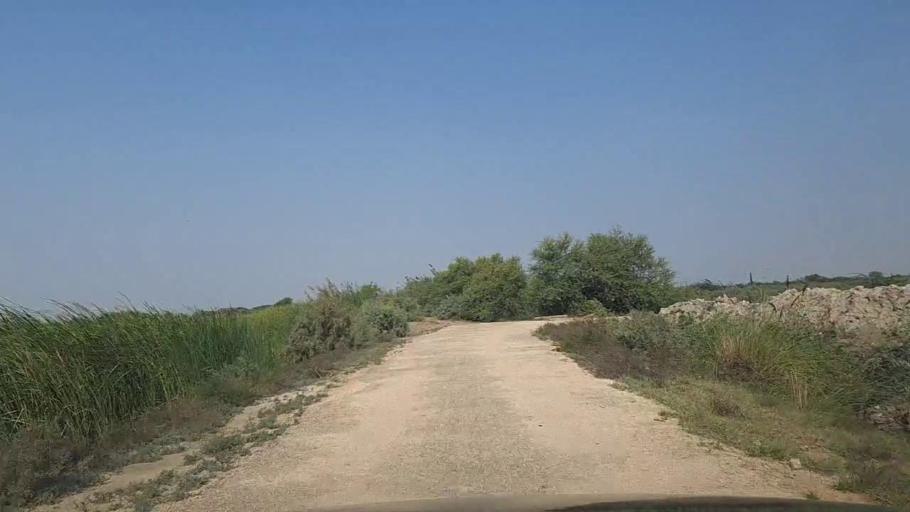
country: PK
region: Sindh
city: Mirpur Sakro
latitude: 24.6215
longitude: 67.7867
